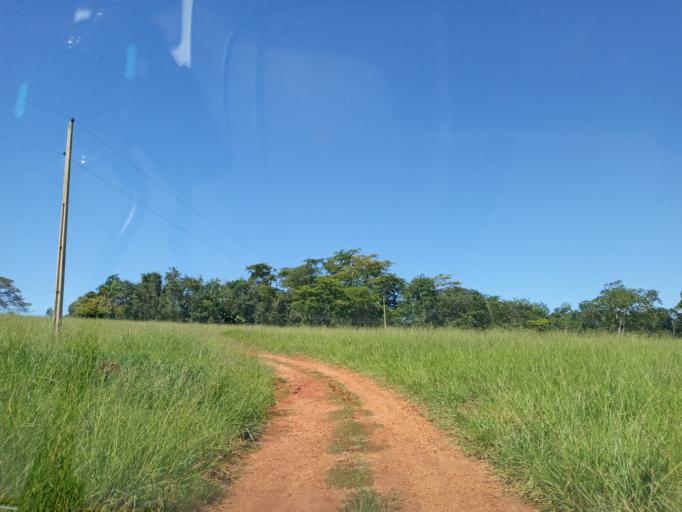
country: BR
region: Goias
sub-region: Itumbiara
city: Itumbiara
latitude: -18.4029
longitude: -49.1421
